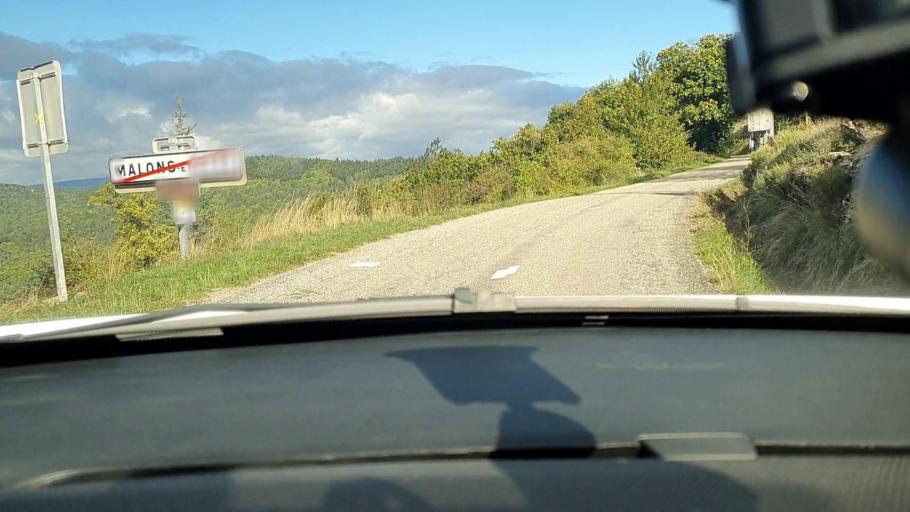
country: FR
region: Rhone-Alpes
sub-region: Departement de l'Ardeche
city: Les Vans
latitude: 44.4161
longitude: 4.0218
